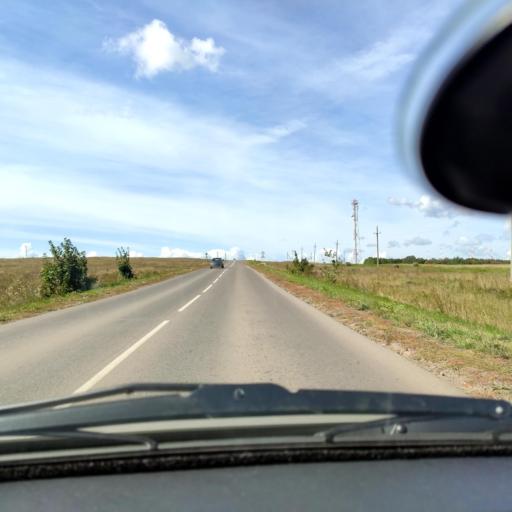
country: RU
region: Bashkortostan
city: Iglino
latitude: 54.9011
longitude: 56.1833
